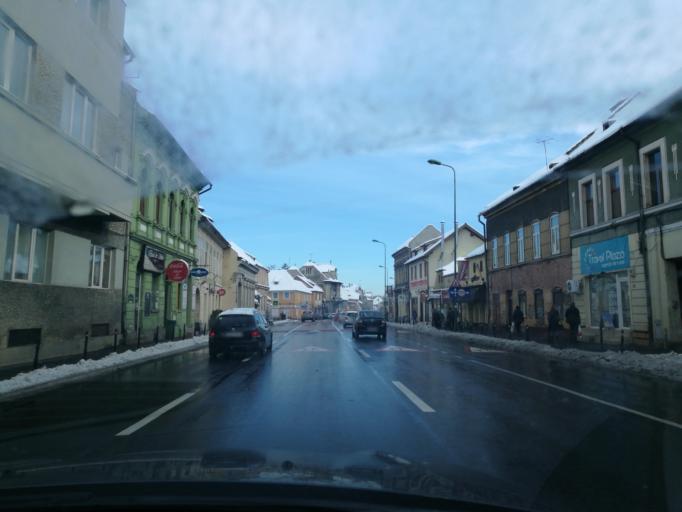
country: RO
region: Brasov
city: Brasov
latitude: 45.6462
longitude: 25.6002
